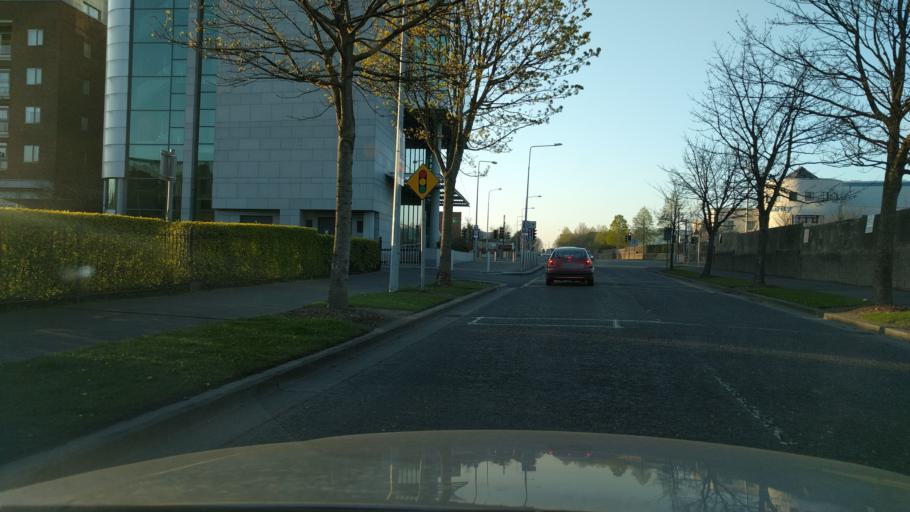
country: IE
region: Leinster
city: Tallaght
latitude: 53.2880
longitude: -6.3691
